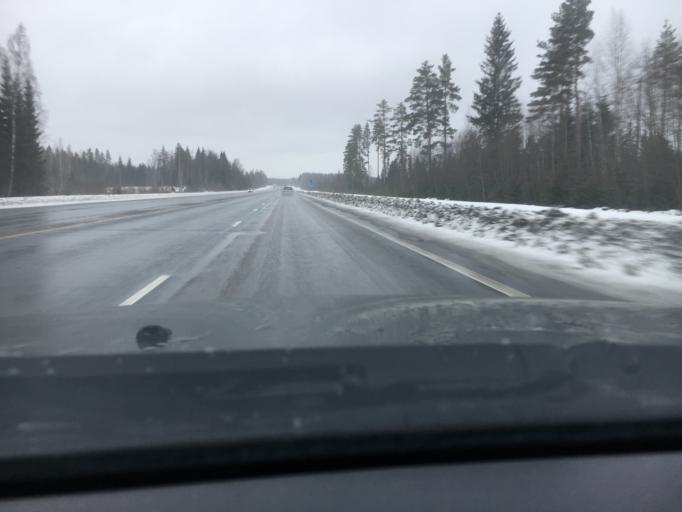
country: FI
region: Central Finland
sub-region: Joutsa
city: Joutsa
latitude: 61.7706
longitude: 26.1012
